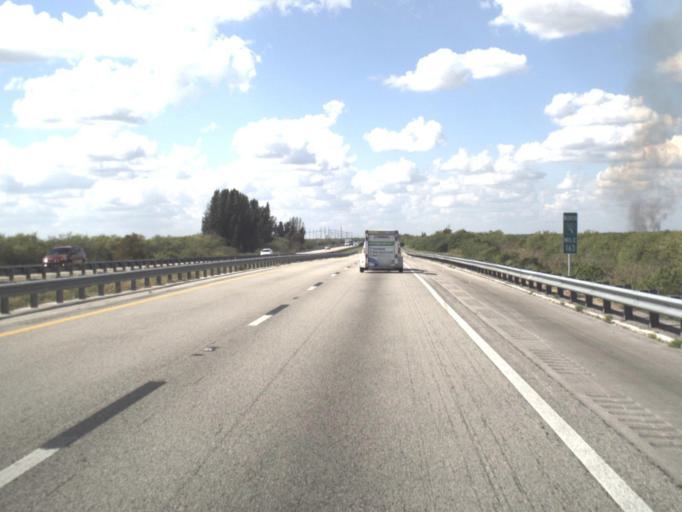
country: US
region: Florida
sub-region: Saint Lucie County
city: Lakewood Park
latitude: 27.4851
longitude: -80.5185
